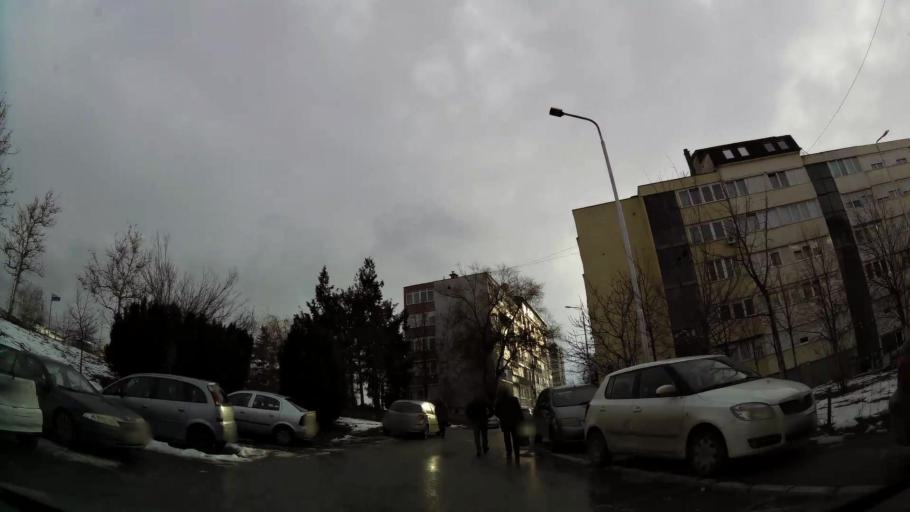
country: XK
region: Pristina
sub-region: Komuna e Prishtines
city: Pristina
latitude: 42.6533
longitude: 21.1636
